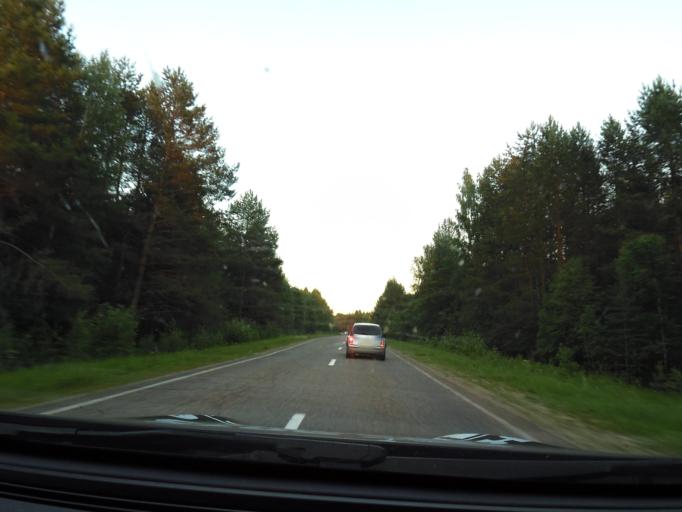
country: RU
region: Jaroslavl
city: Lyubim
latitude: 58.3469
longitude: 40.8219
